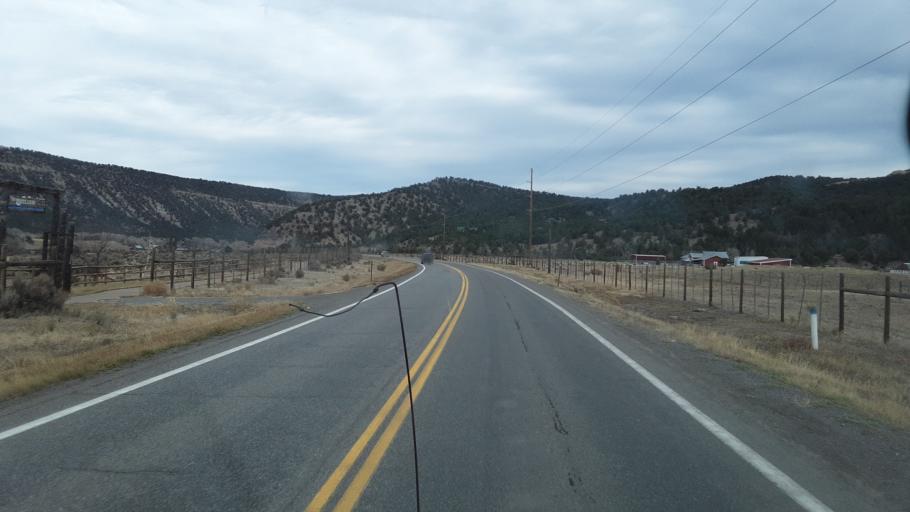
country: US
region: Colorado
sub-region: Ouray County
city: Ouray
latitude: 38.1746
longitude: -107.7417
